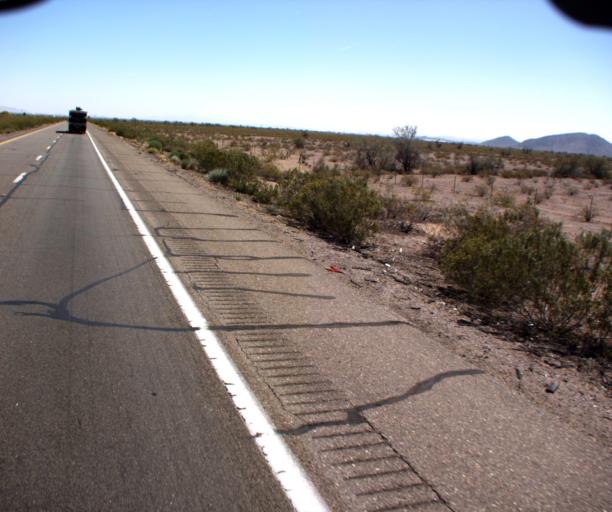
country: US
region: Arizona
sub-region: Maricopa County
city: Buckeye
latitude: 33.5058
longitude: -112.9842
